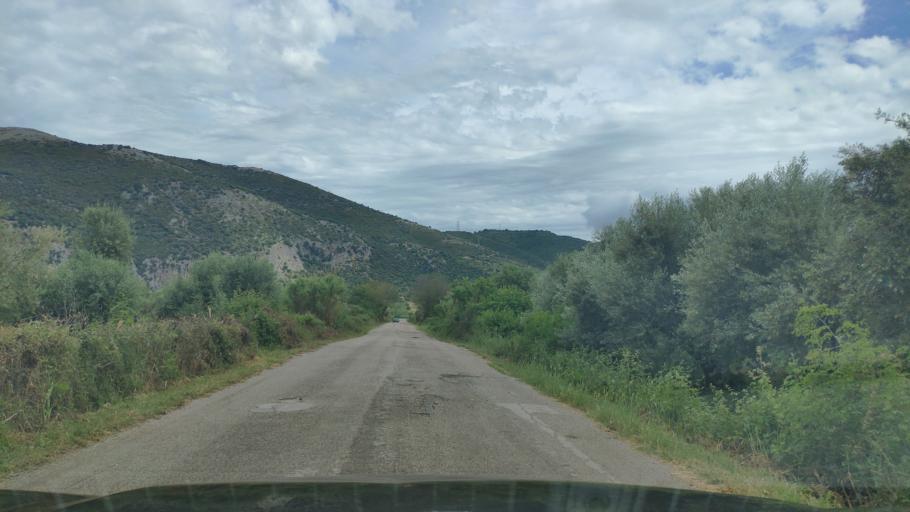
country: GR
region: West Greece
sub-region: Nomos Aitolias kai Akarnanias
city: Vonitsa
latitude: 38.9101
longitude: 20.9004
